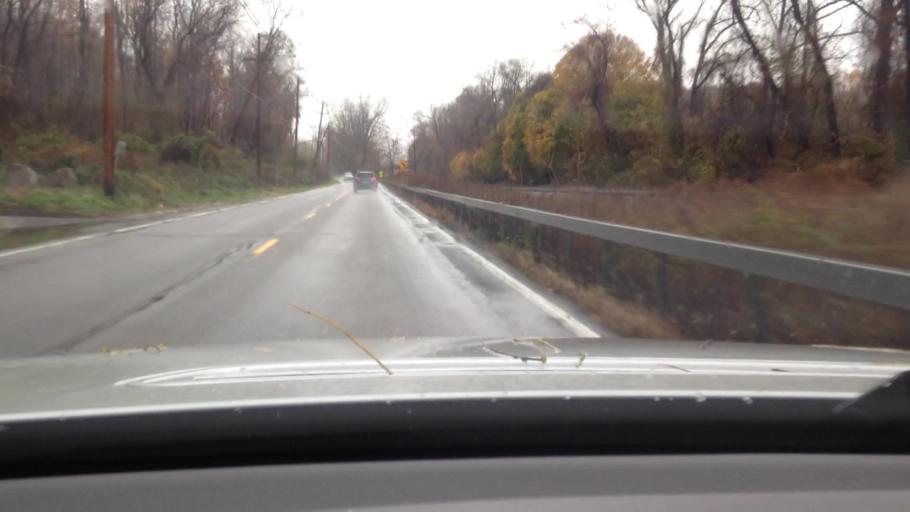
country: US
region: New York
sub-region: Putnam County
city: Cold Spring
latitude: 41.4298
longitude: -73.9681
